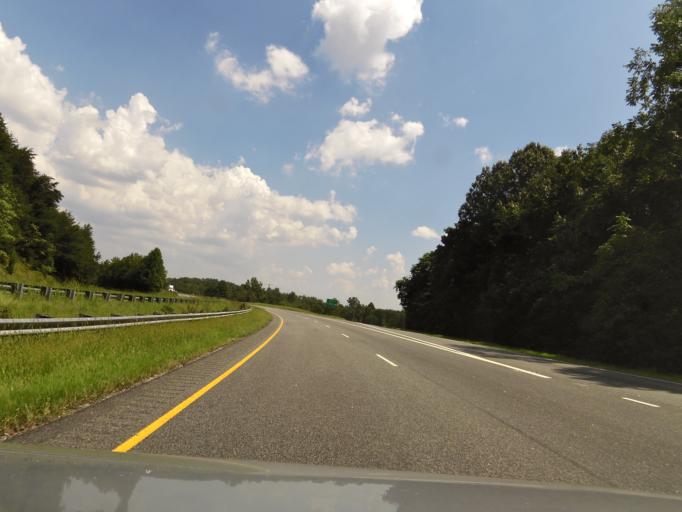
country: US
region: North Carolina
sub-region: Polk County
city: Columbus
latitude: 35.2588
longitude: -82.1875
